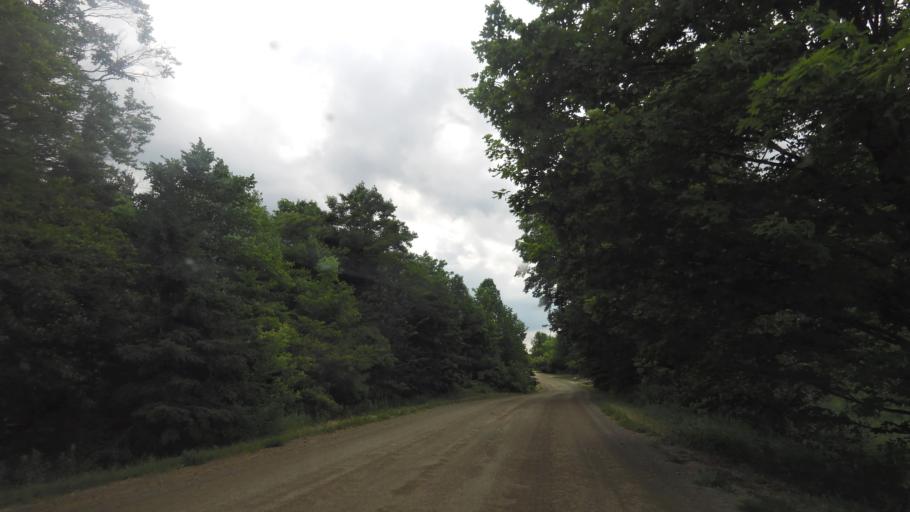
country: CA
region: Ontario
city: Orangeville
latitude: 43.8554
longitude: -79.9526
